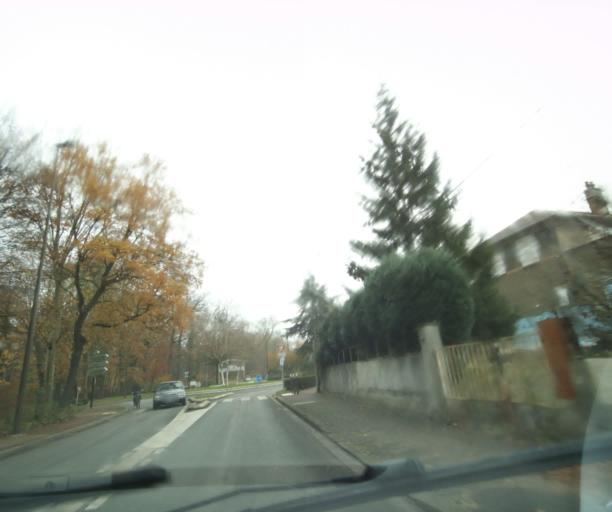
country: FR
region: Ile-de-France
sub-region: Departement de Seine-Saint-Denis
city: Livry-Gargan
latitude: 48.9337
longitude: 2.5530
